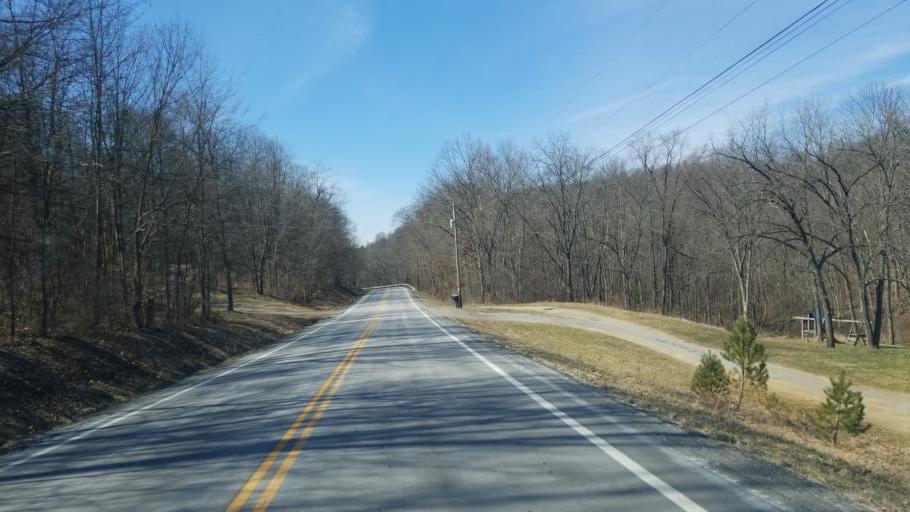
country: US
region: Ohio
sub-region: Knox County
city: Oak Hill
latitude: 40.4633
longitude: -82.1362
